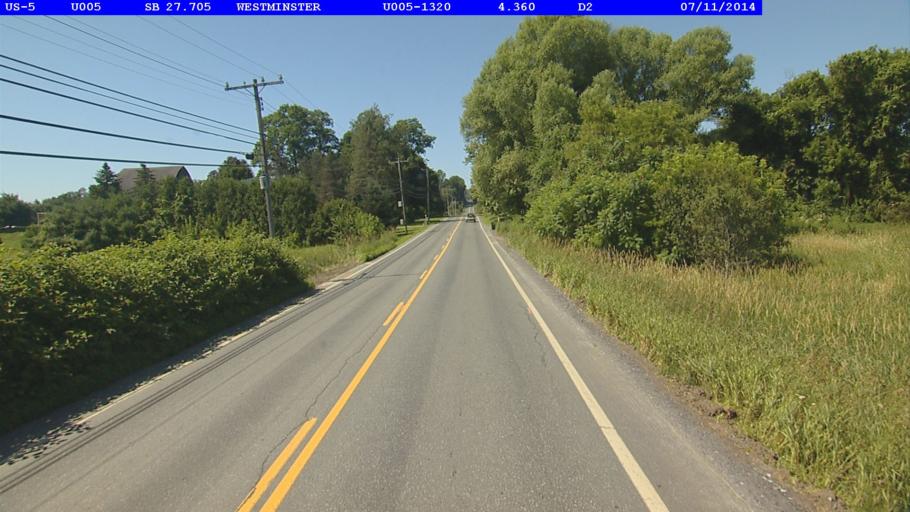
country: US
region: Vermont
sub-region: Windham County
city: Bellows Falls
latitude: 43.0766
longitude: -72.4488
